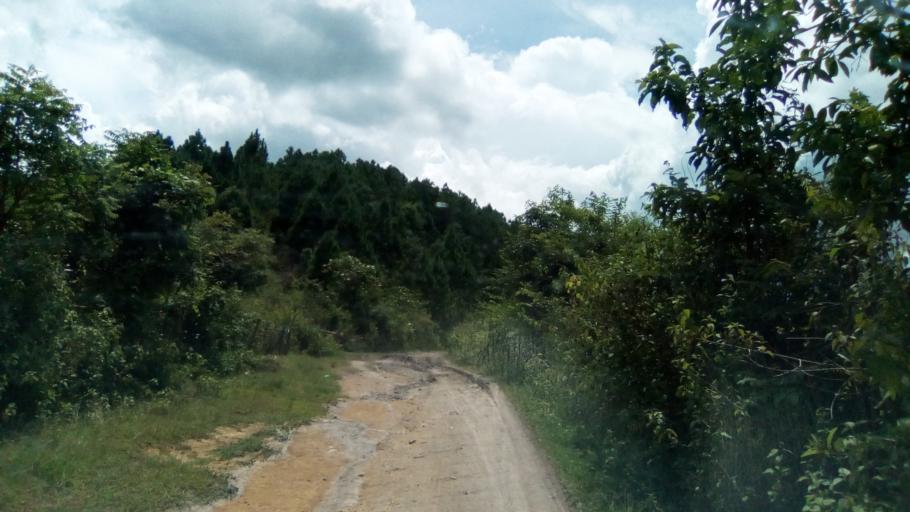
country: LA
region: Xiangkhoang
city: Muang Phonsavan
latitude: 19.3397
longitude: 103.6259
